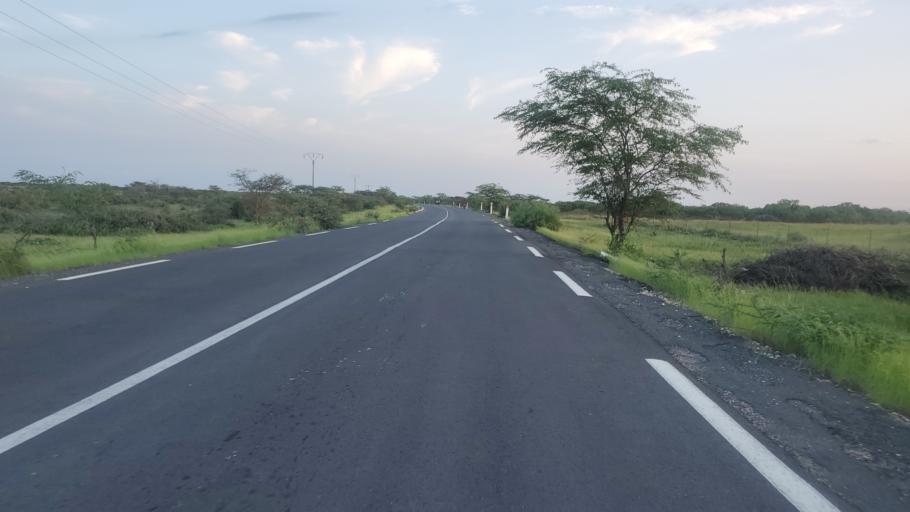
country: SN
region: Saint-Louis
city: Saint-Louis
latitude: 16.1219
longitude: -16.4142
